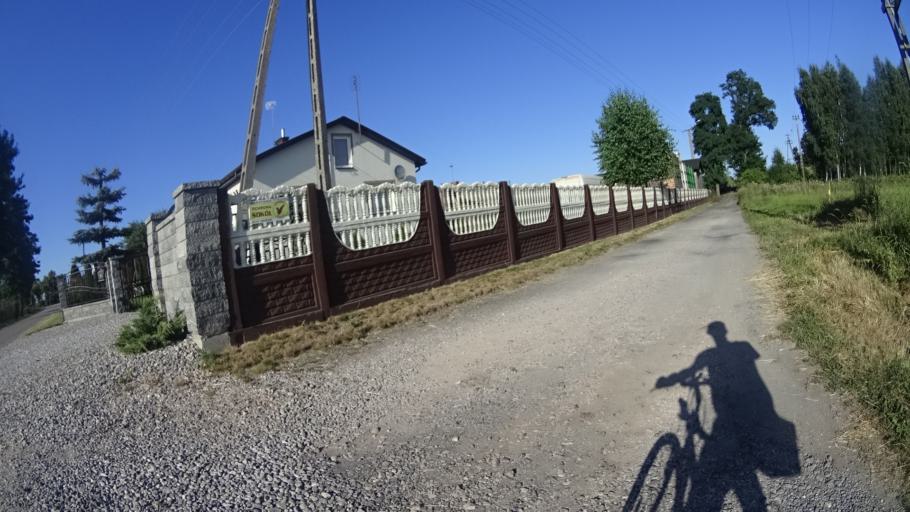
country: PL
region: Masovian Voivodeship
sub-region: Powiat bialobrzeski
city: Wysmierzyce
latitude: 51.6735
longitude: 20.8310
